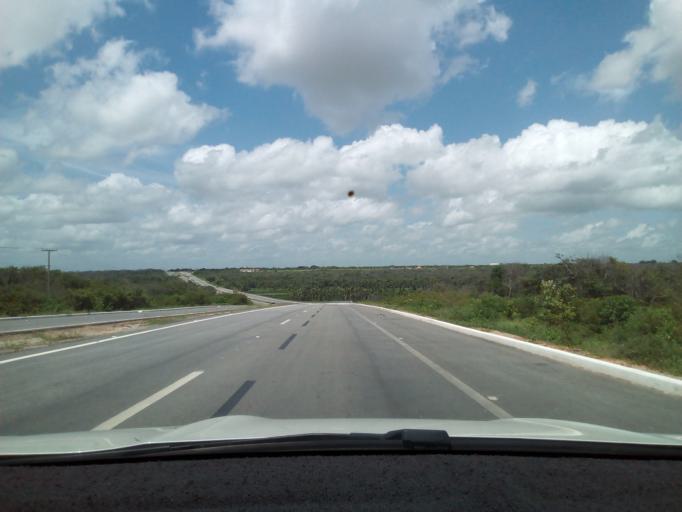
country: BR
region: Ceara
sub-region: Aracati
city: Aracati
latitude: -4.5460
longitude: -37.7990
